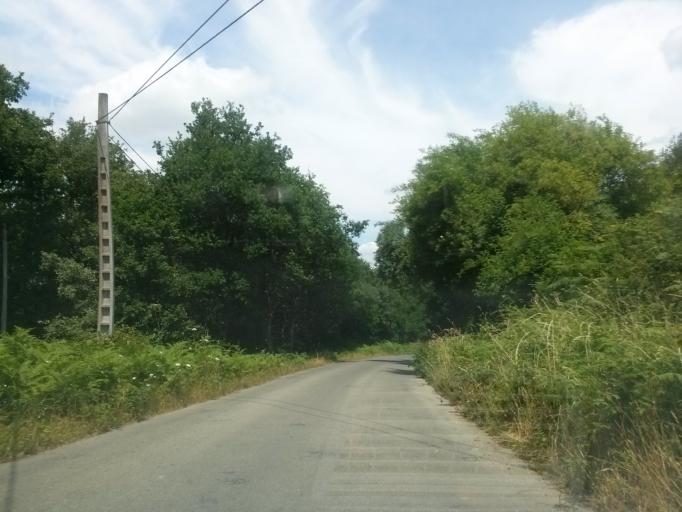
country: ES
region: Galicia
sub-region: Provincia de Lugo
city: Outeiro de Rei
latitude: 43.0414
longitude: -7.6143
